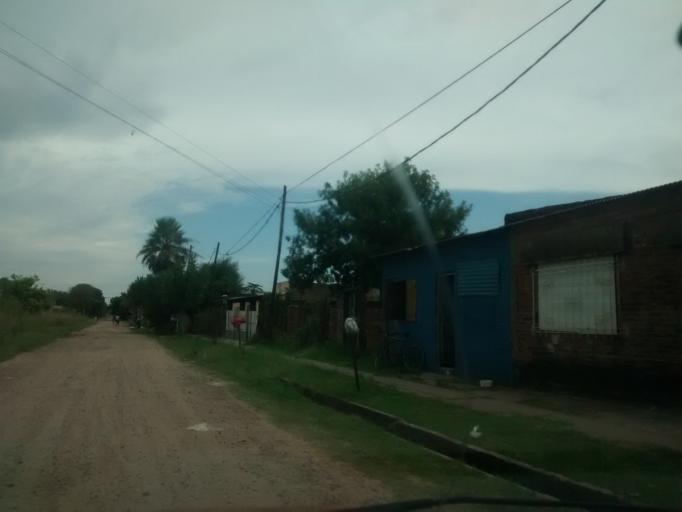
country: AR
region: Chaco
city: Fontana
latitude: -27.4520
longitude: -59.0212
